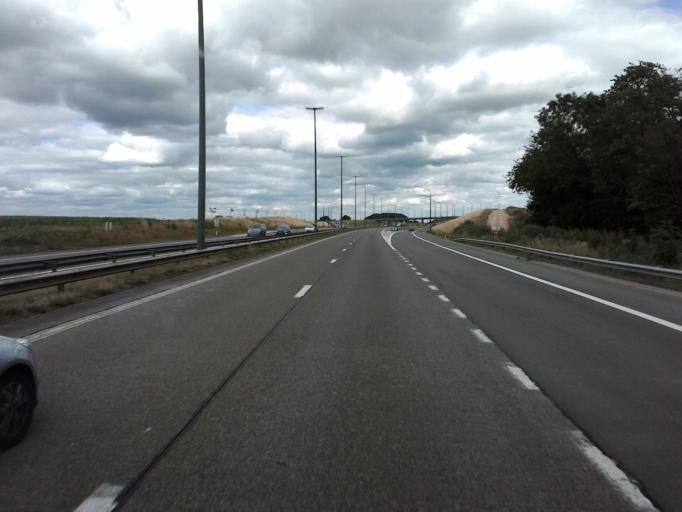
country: LU
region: Luxembourg
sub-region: Canton de Capellen
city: Clemency
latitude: 49.6398
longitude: 5.8794
